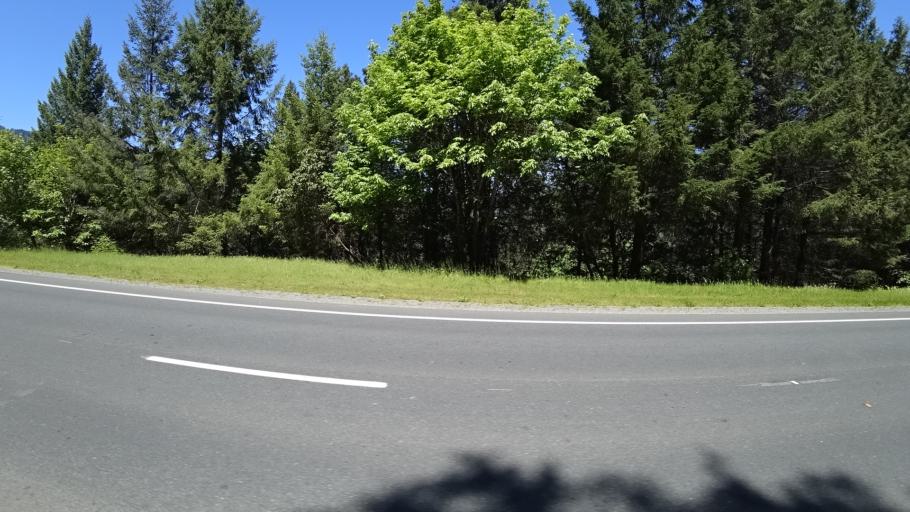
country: US
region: California
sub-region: Humboldt County
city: Willow Creek
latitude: 40.9422
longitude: -123.6403
